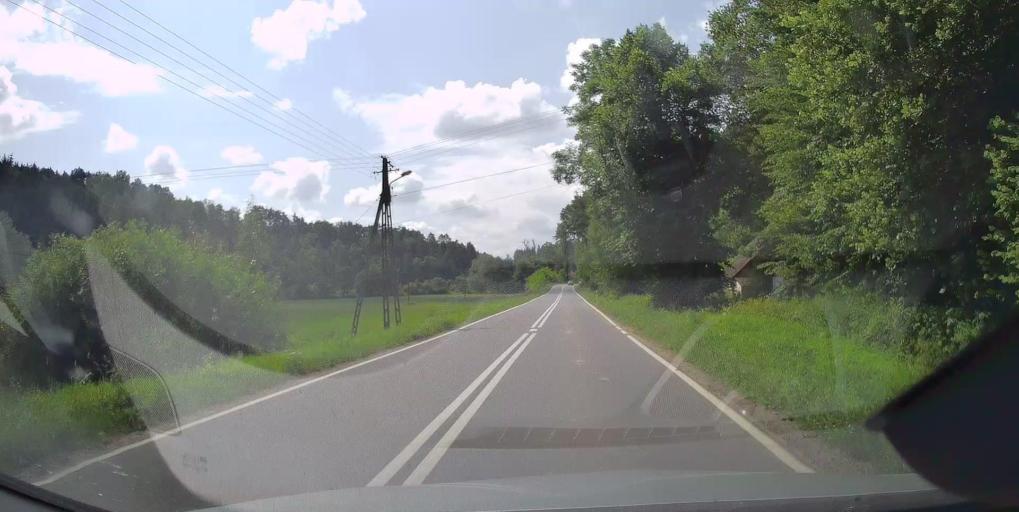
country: PL
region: Lesser Poland Voivodeship
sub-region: Powiat tarnowski
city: Zakliczyn
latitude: 49.8040
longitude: 20.7978
